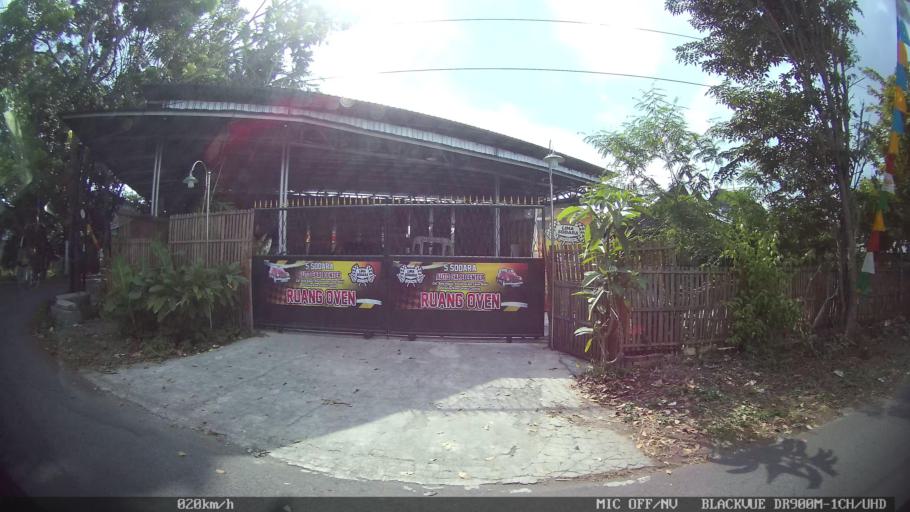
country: ID
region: Daerah Istimewa Yogyakarta
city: Gamping Lor
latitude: -7.7890
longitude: 110.3379
